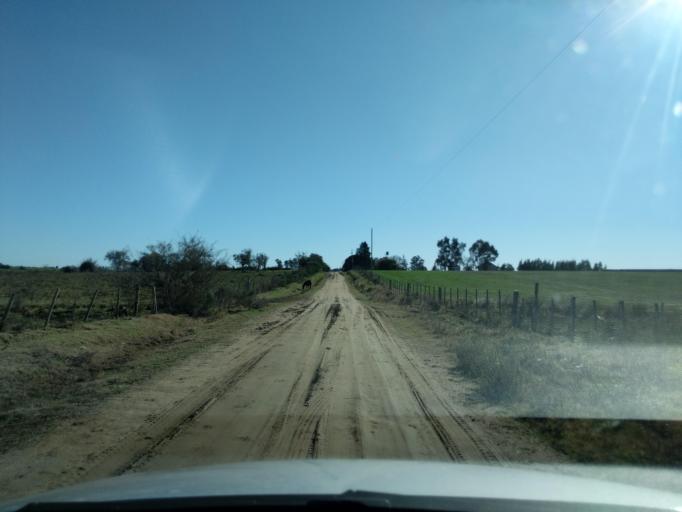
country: UY
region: Florida
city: Florida
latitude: -34.0730
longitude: -56.2676
